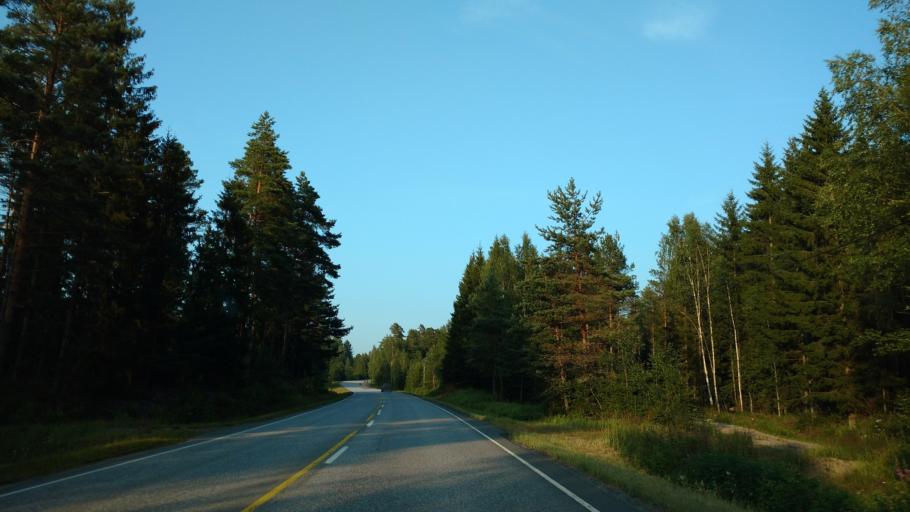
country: FI
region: Varsinais-Suomi
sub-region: Salo
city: Saerkisalo
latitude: 60.1767
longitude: 22.9223
